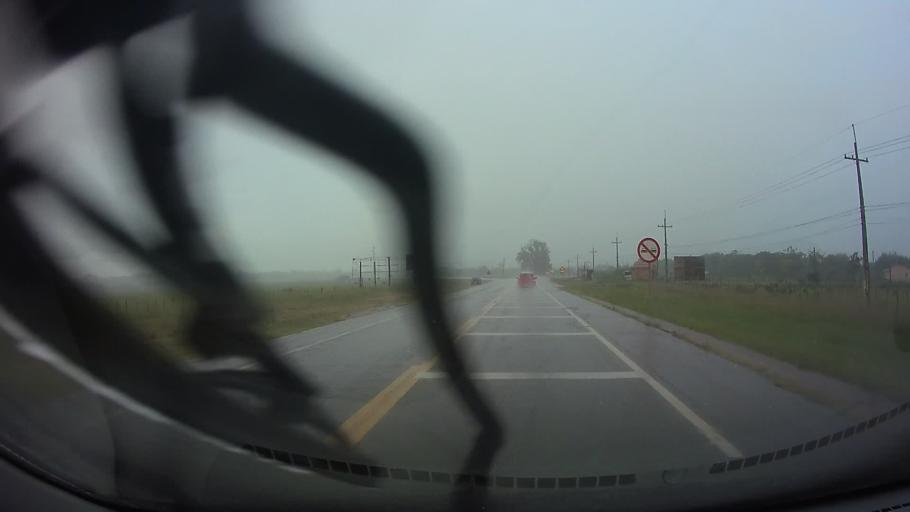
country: PY
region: Paraguari
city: Paraguari
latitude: -25.6393
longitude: -57.1553
